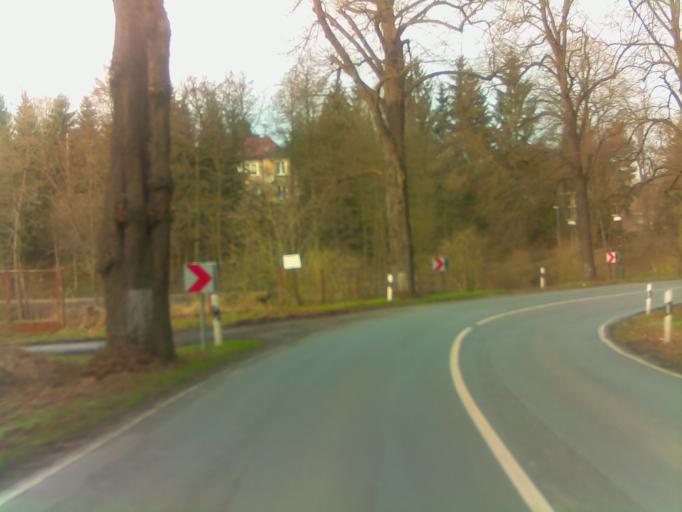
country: DE
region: Thuringia
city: Stadtroda
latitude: 50.8499
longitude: 11.7265
